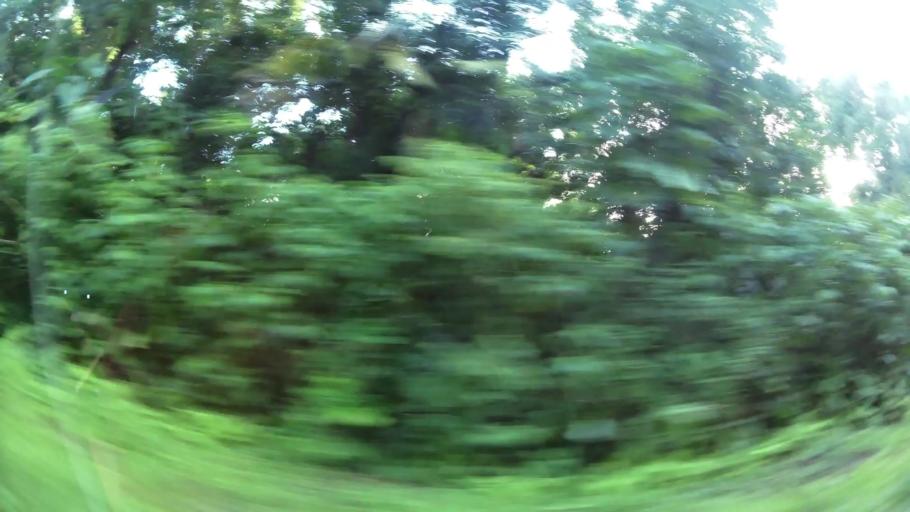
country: GP
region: Guadeloupe
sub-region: Guadeloupe
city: Bouillante
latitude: 16.1759
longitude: -61.7014
